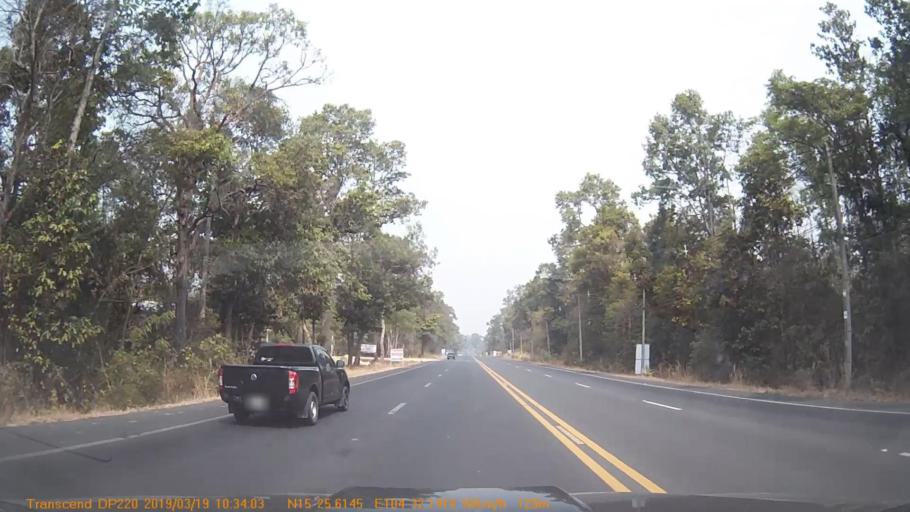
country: TH
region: Changwat Ubon Ratchathani
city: Khueang Nai
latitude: 15.4272
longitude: 104.5355
